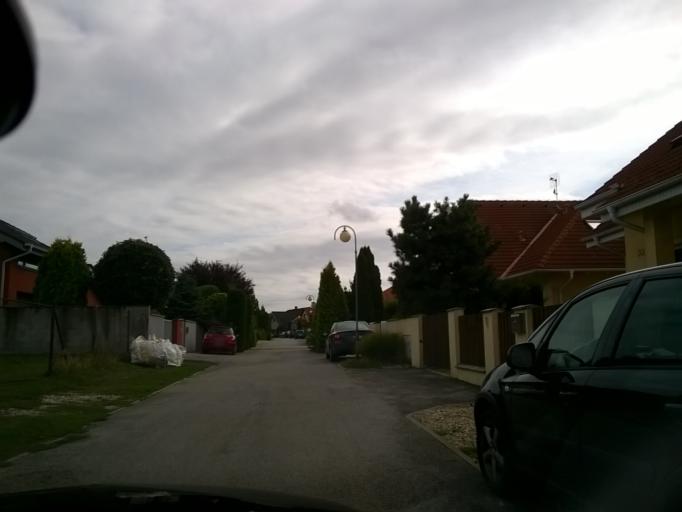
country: SK
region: Nitriansky
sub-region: Okres Nitra
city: Nitra
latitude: 48.2965
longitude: 18.0517
